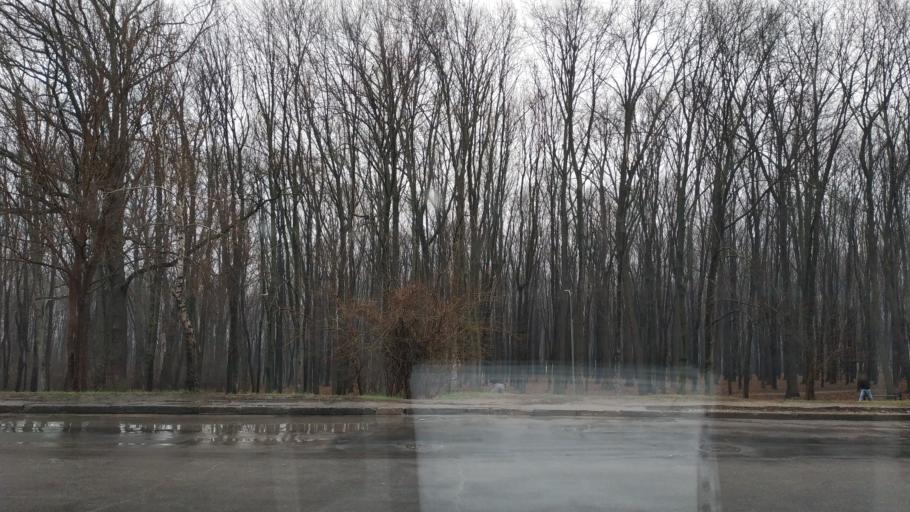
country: MD
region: Chisinau
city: Vatra
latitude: 47.0375
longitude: 28.7833
